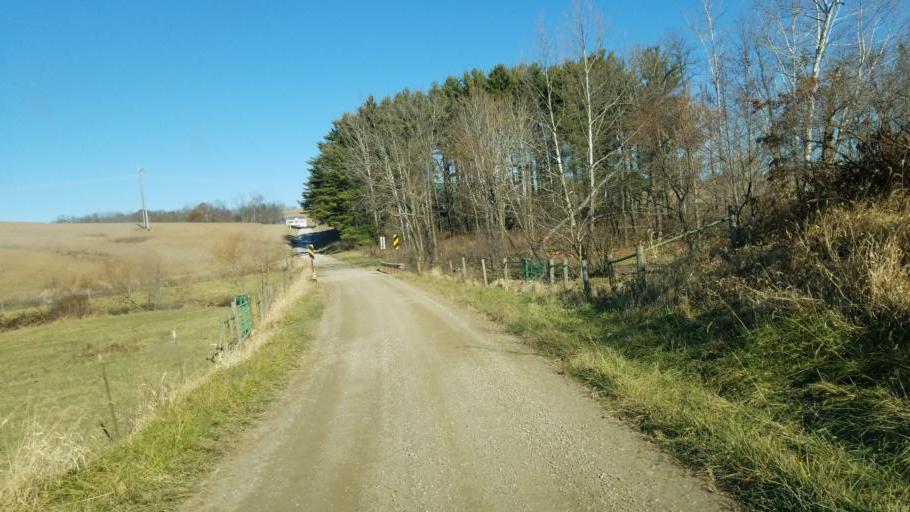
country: US
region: Ohio
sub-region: Muskingum County
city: Dresden
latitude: 40.1000
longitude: -81.9600
